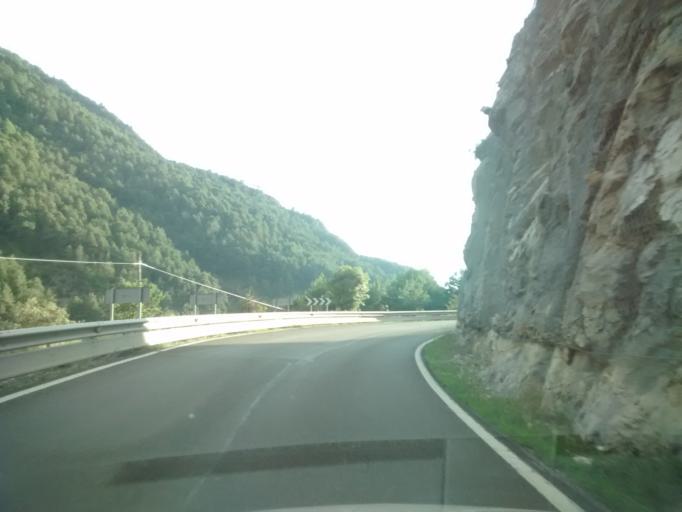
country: ES
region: Aragon
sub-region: Provincia de Huesca
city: Boltana
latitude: 42.4676
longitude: 0.0166
